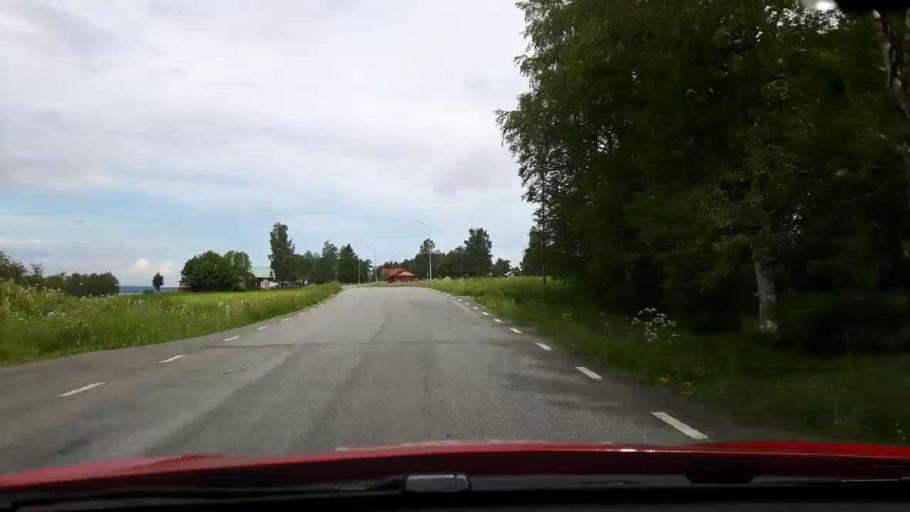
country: SE
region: Jaemtland
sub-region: OEstersunds Kommun
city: Ostersund
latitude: 63.0450
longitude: 14.4555
